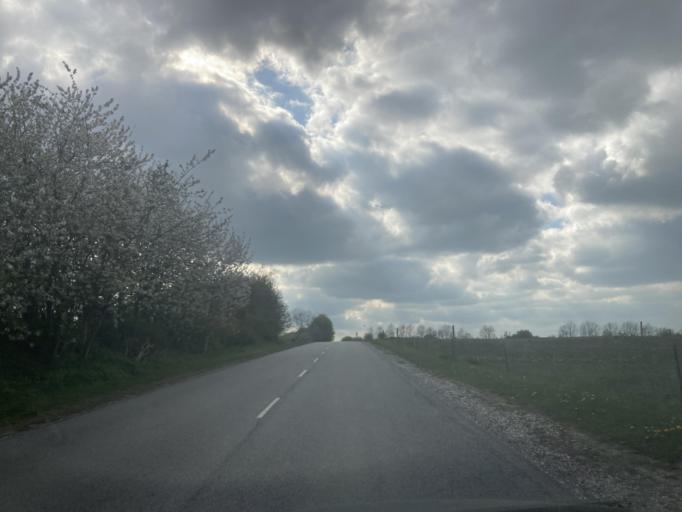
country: DK
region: Zealand
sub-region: Greve Kommune
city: Tune
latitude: 55.6000
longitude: 12.1757
